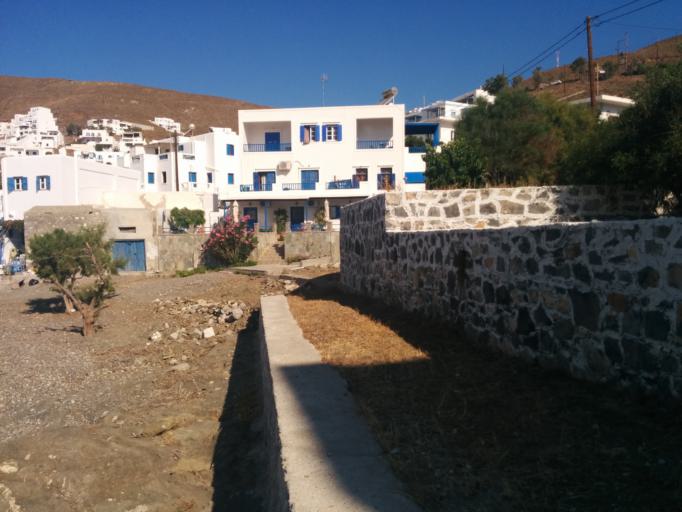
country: GR
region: South Aegean
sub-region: Nomos Dodekanisou
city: Astypalaia
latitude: 36.5491
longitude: 26.3537
